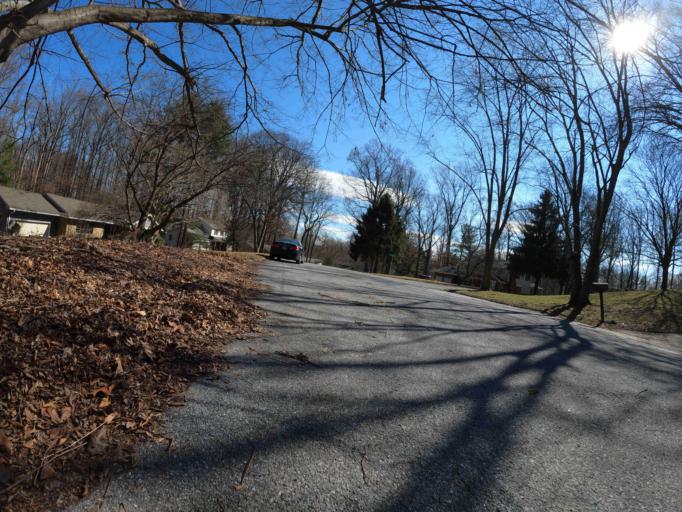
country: US
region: Maryland
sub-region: Howard County
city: Columbia
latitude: 39.2917
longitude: -76.8481
